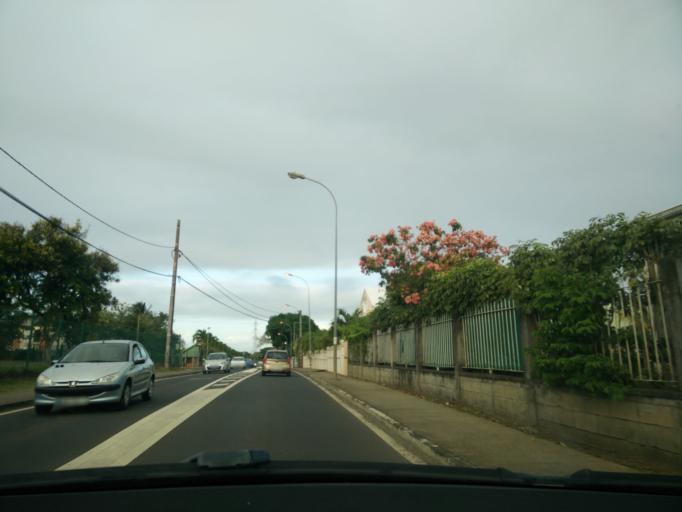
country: GP
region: Guadeloupe
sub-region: Guadeloupe
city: Baie-Mahault
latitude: 16.2411
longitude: -61.5943
